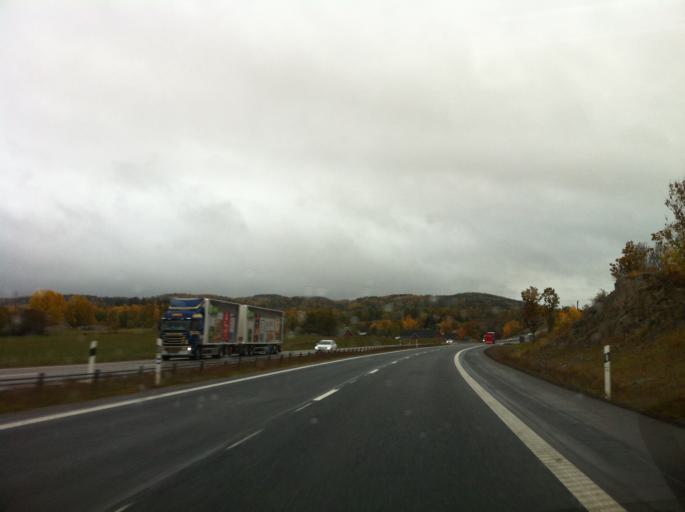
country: SE
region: Joenkoeping
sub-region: Jonkopings Kommun
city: Kaxholmen
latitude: 57.9389
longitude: 14.3333
